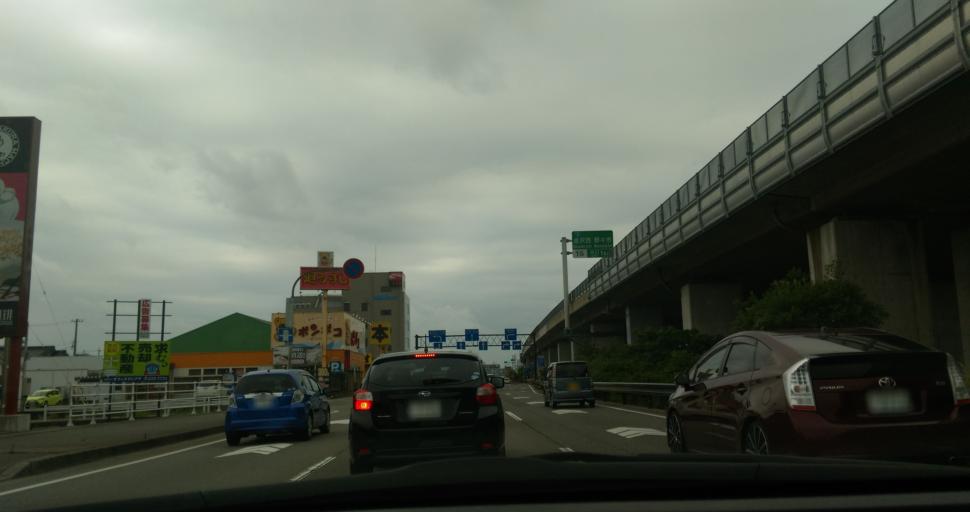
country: JP
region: Ishikawa
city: Kanazawa-shi
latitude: 36.5805
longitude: 136.6191
